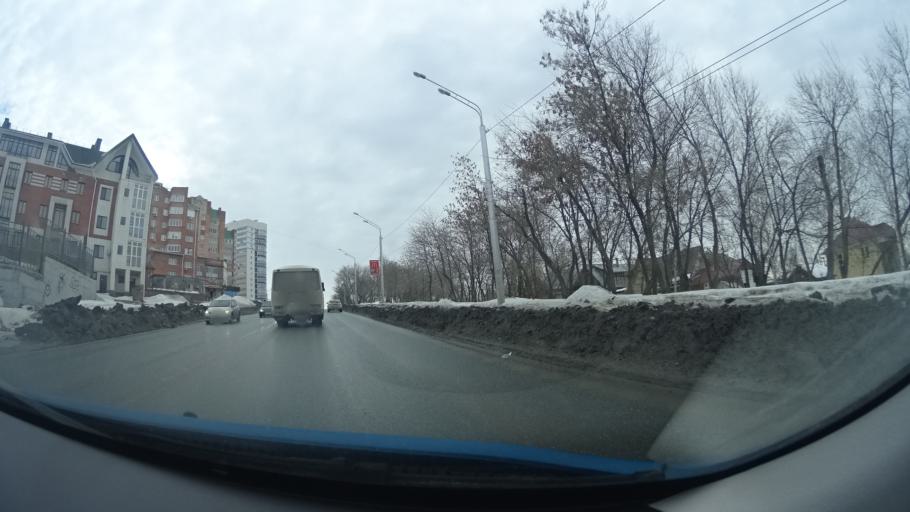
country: RU
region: Bashkortostan
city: Ufa
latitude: 54.7038
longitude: 55.9758
